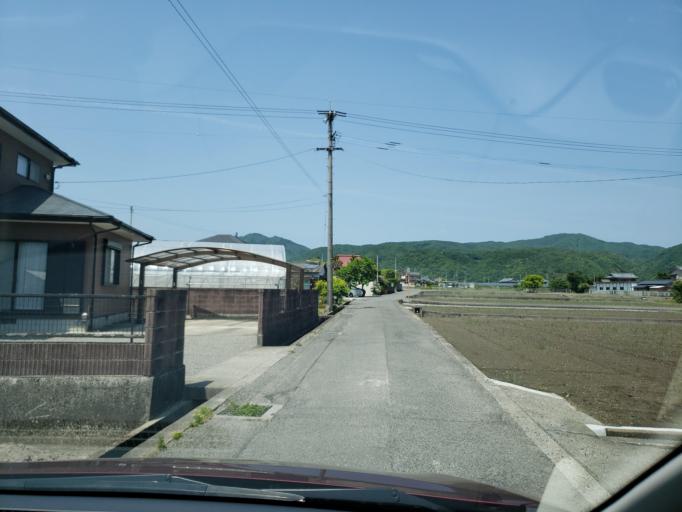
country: JP
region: Tokushima
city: Kamojimacho-jogejima
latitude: 34.0959
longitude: 134.2683
